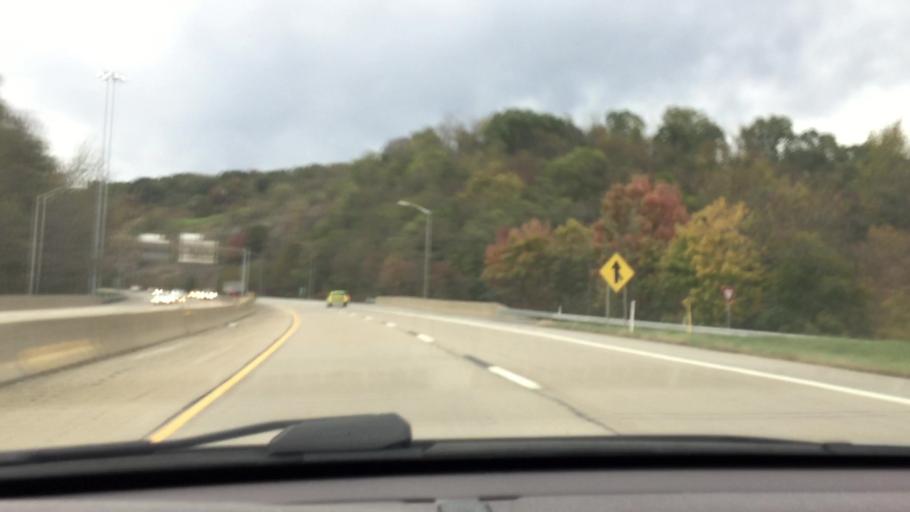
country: US
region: Pennsylvania
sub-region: Beaver County
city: Beaver
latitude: 40.6845
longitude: -80.3348
